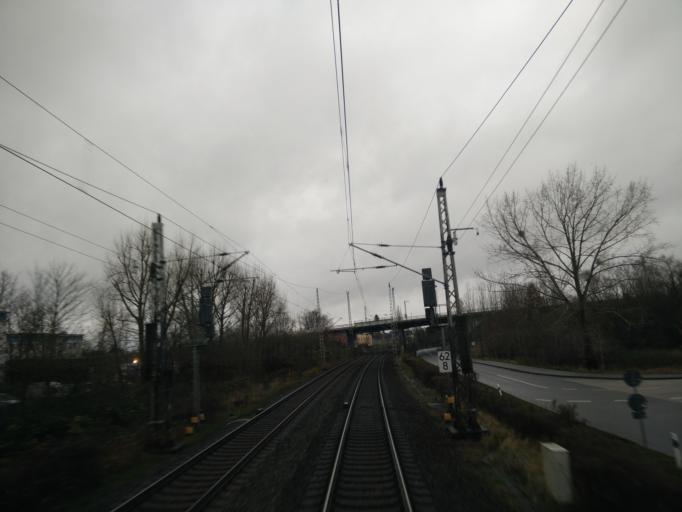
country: DE
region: Mecklenburg-Vorpommern
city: Feldstadt
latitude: 53.6066
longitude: 11.3840
